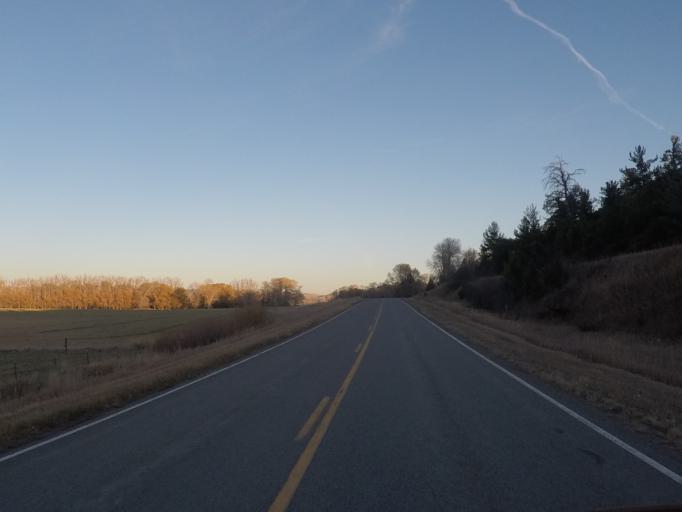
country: US
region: Montana
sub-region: Sweet Grass County
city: Big Timber
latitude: 45.7853
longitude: -109.8456
